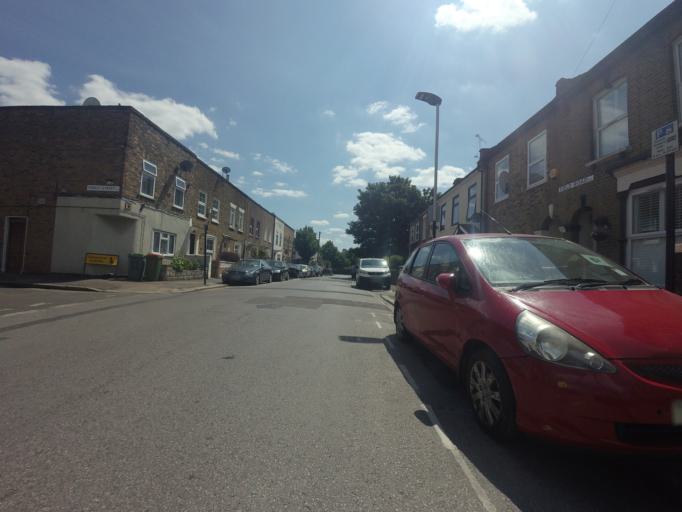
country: GB
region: England
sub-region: Greater London
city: East Ham
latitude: 51.5497
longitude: 0.0204
